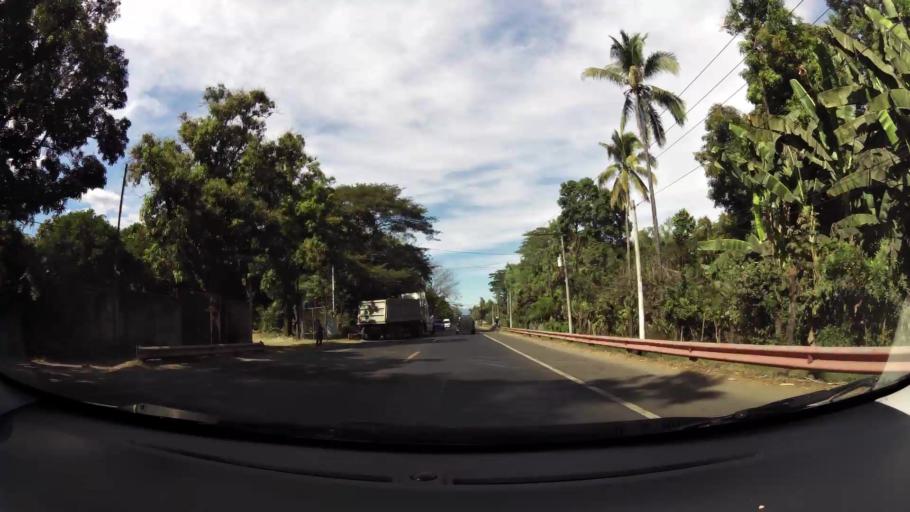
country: SV
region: San Salvador
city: Aguilares
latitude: 13.9272
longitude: -89.1856
